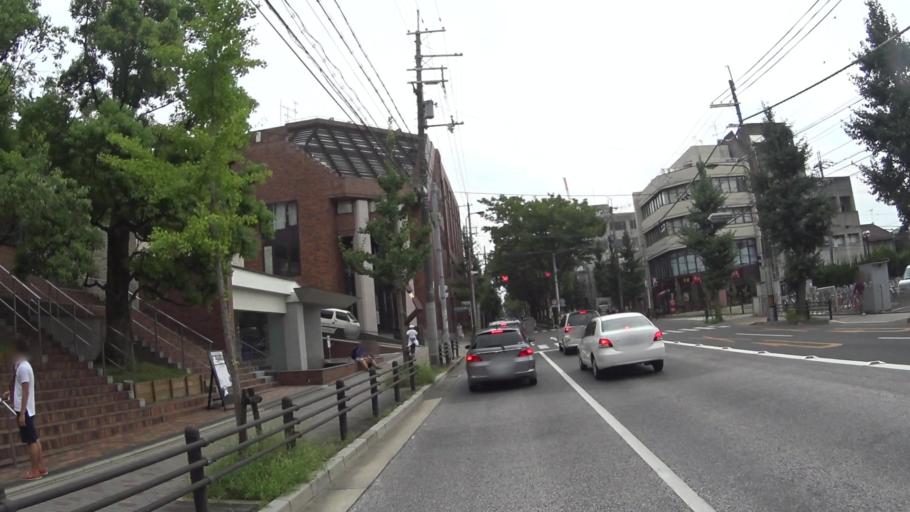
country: JP
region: Kyoto
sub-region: Kyoto-shi
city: Kamigyo-ku
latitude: 35.0370
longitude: 135.7917
